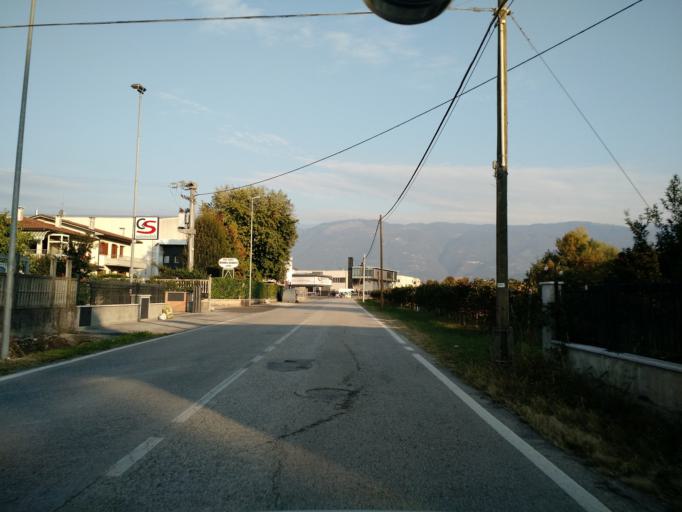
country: IT
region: Veneto
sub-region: Provincia di Vicenza
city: Breganze
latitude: 45.7093
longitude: 11.5455
